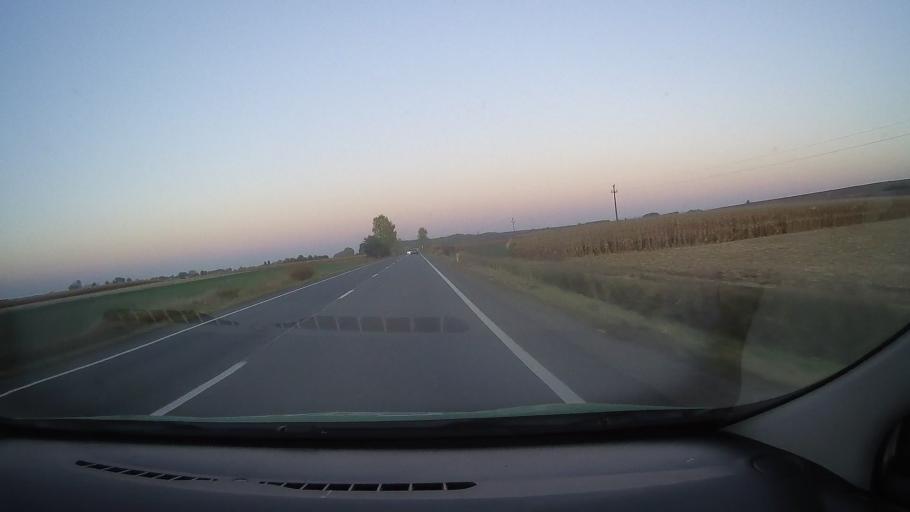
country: RO
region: Bihor
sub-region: Comuna Tarcea
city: Tarcea
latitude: 47.4256
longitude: 22.1974
